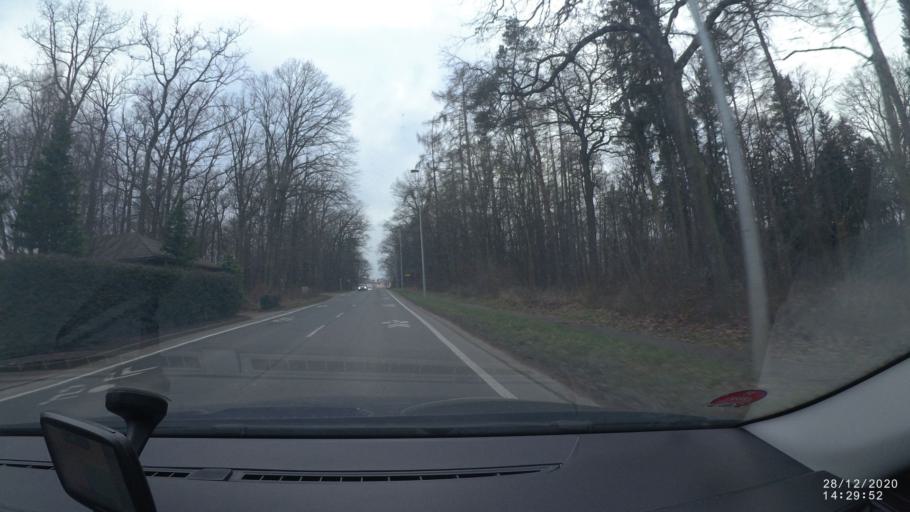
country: CZ
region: Central Bohemia
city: Sestajovice
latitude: 50.0800
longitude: 14.6609
